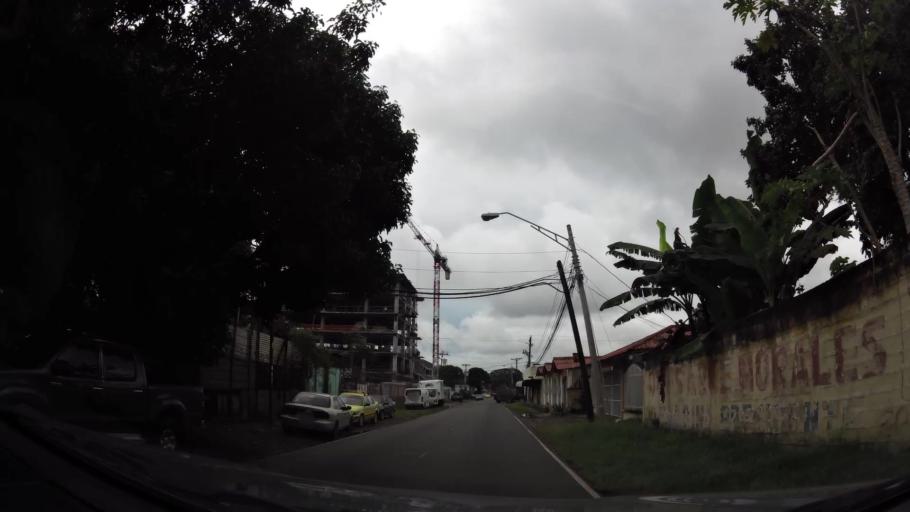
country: PA
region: Chiriqui
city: David
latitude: 8.4331
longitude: -82.4273
